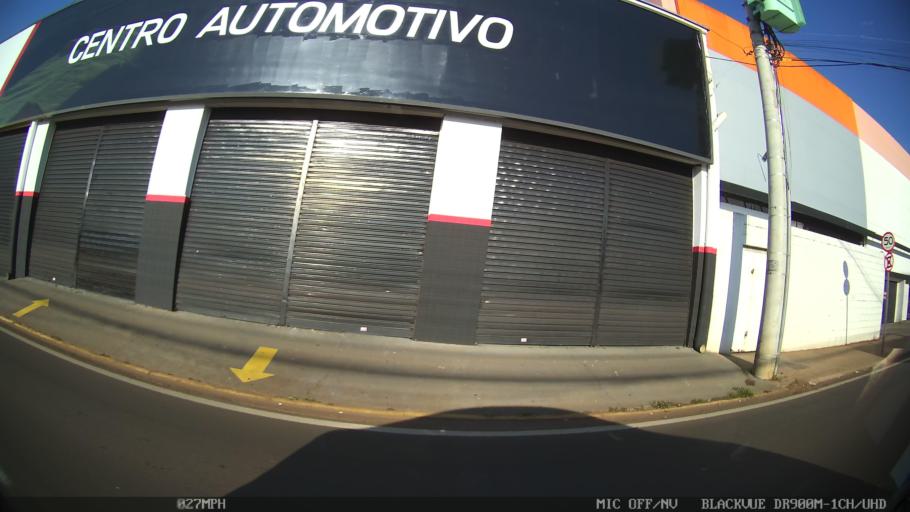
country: BR
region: Sao Paulo
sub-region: Piracicaba
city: Piracicaba
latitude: -22.7096
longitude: -47.6548
